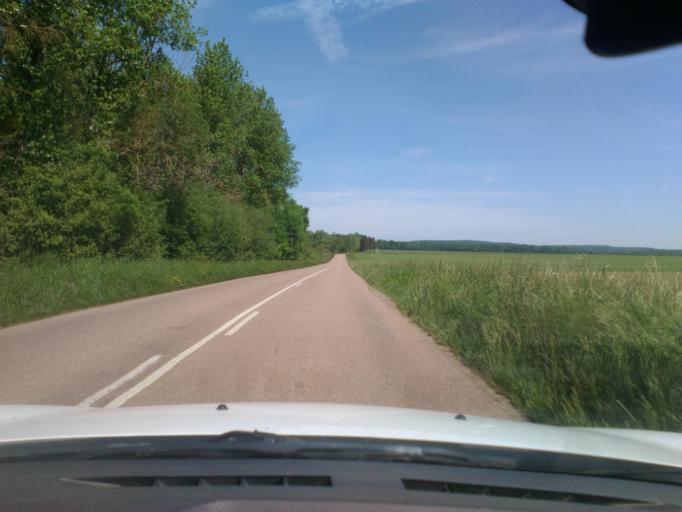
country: FR
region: Lorraine
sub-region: Departement des Vosges
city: Rambervillers
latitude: 48.4071
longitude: 6.5873
